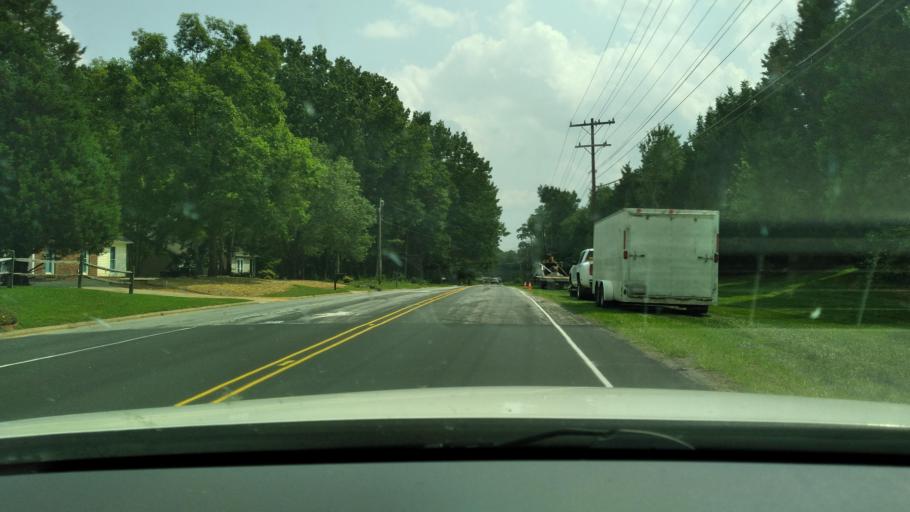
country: US
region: North Carolina
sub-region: Guilford County
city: Jamestown
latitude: 36.0455
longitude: -79.8906
